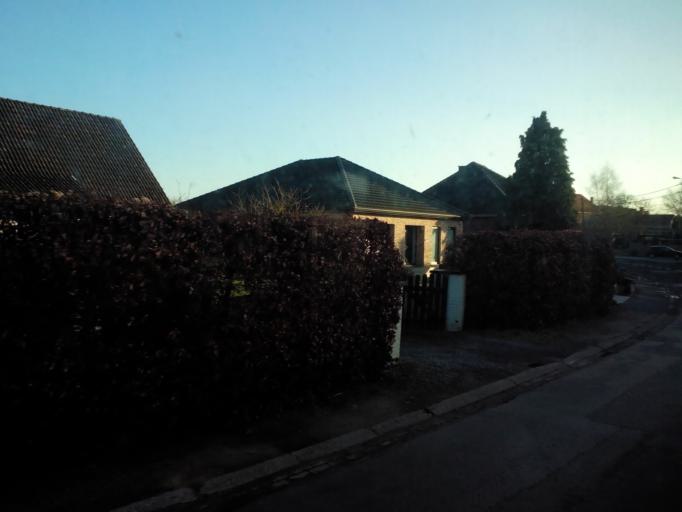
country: BE
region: Flanders
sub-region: Provincie Vlaams-Brabant
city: Bierbeek
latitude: 50.8365
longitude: 4.7290
